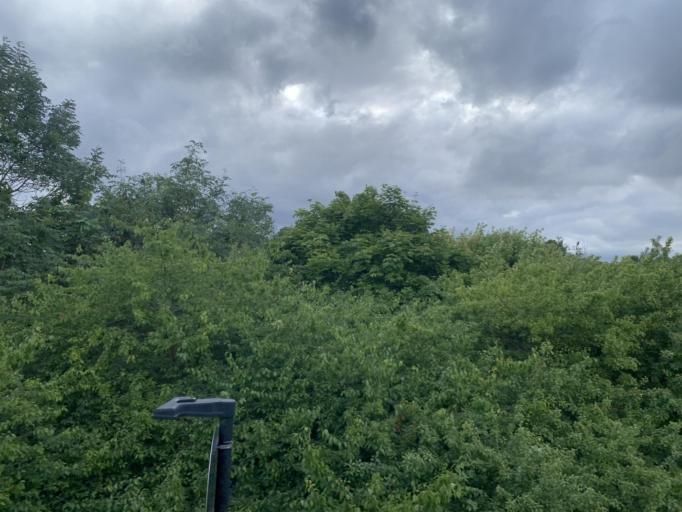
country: GB
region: England
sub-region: West Berkshire
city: Eton
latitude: 51.4853
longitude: -0.6236
